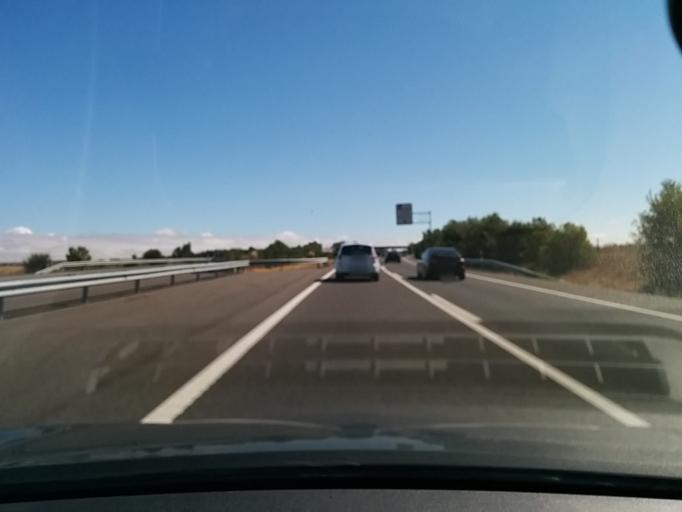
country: ES
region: Aragon
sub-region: Provincia de Huesca
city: Almudebar
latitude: 42.0641
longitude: -0.5256
